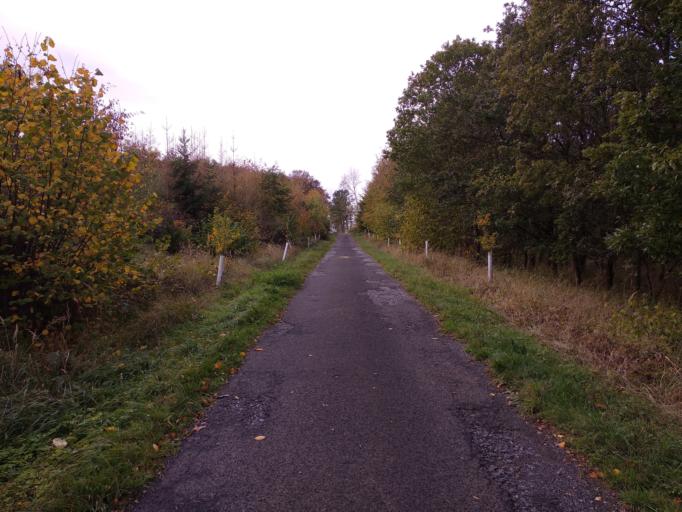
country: DE
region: North Rhine-Westphalia
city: Beverungen
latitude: 51.6698
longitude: 9.3306
